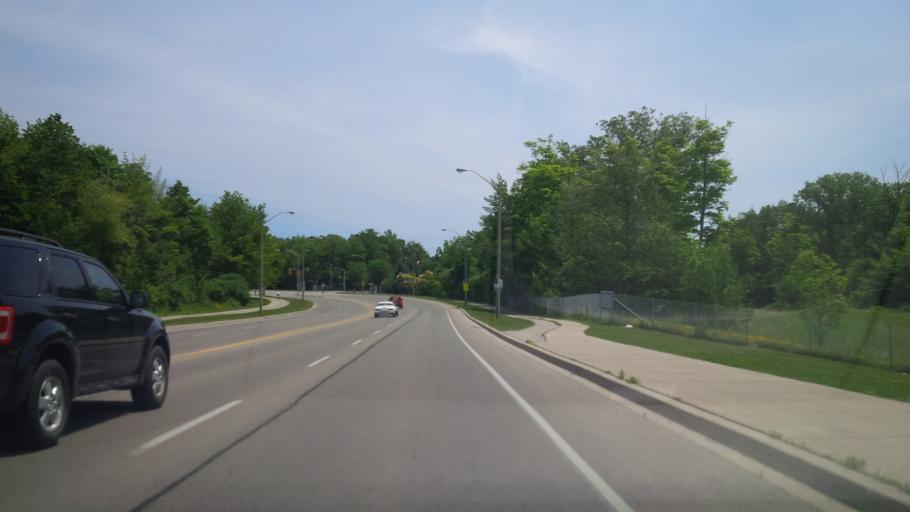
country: CA
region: Ontario
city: Burlington
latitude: 43.3591
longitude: -79.8311
